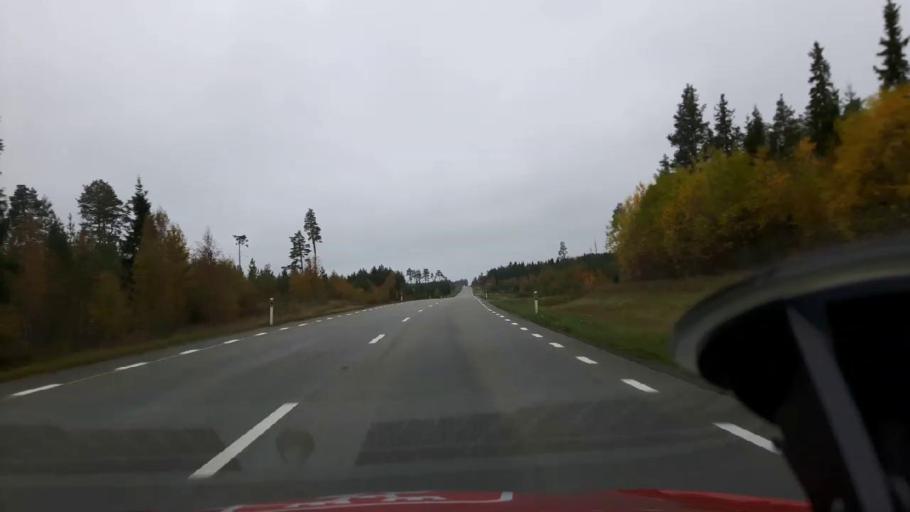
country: SE
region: Jaemtland
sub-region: Bergs Kommun
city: Hoverberg
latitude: 62.7164
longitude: 14.4146
